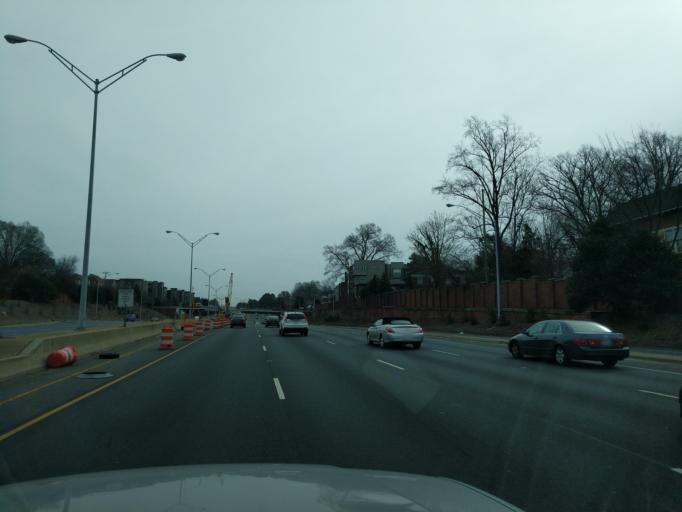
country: US
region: North Carolina
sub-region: Mecklenburg County
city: Charlotte
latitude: 35.2188
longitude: -80.8225
